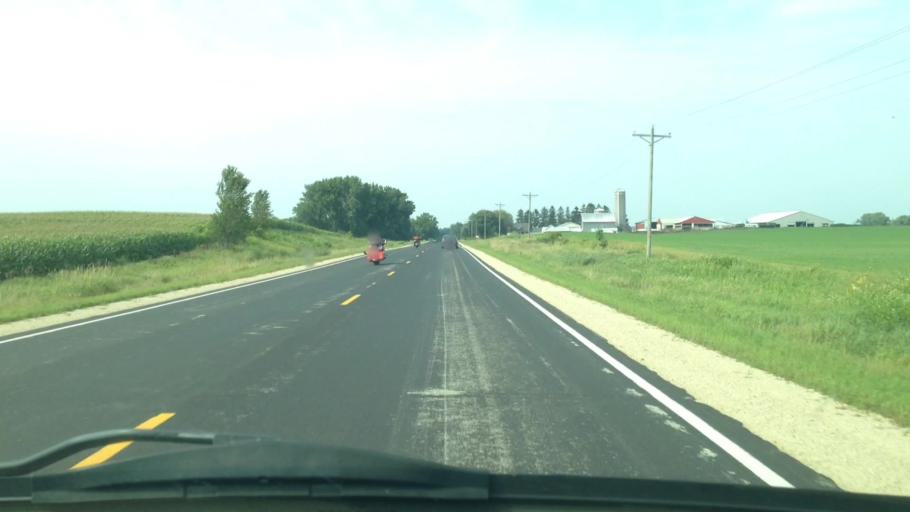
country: US
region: Minnesota
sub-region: Winona County
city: Lewiston
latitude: 43.9542
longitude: -91.9543
